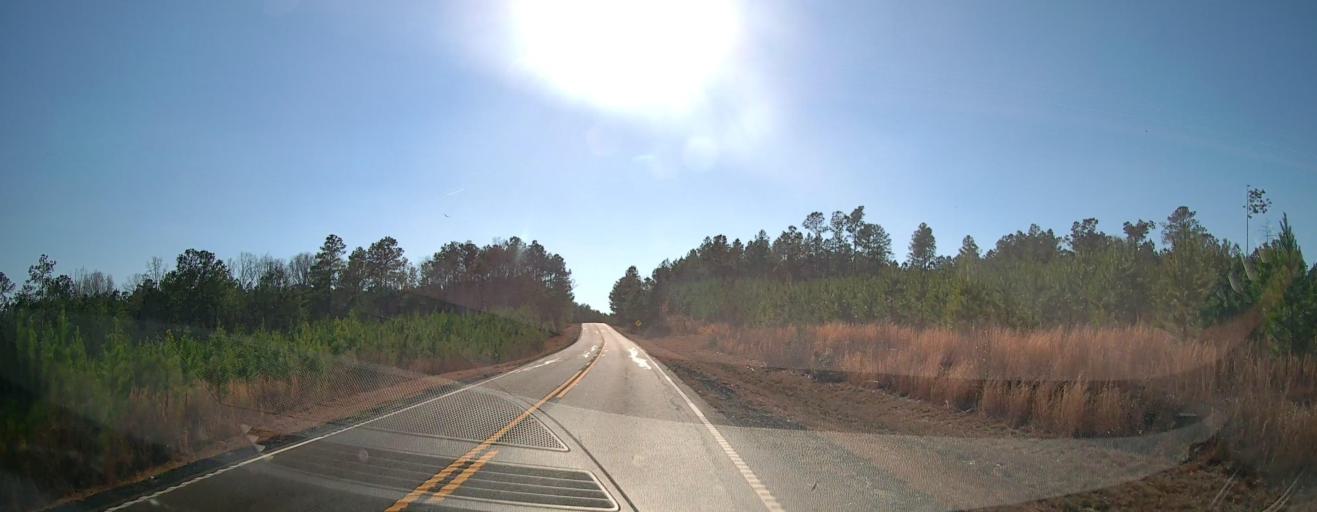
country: US
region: Georgia
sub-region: Talbot County
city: Talbotton
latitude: 32.6486
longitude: -84.4106
